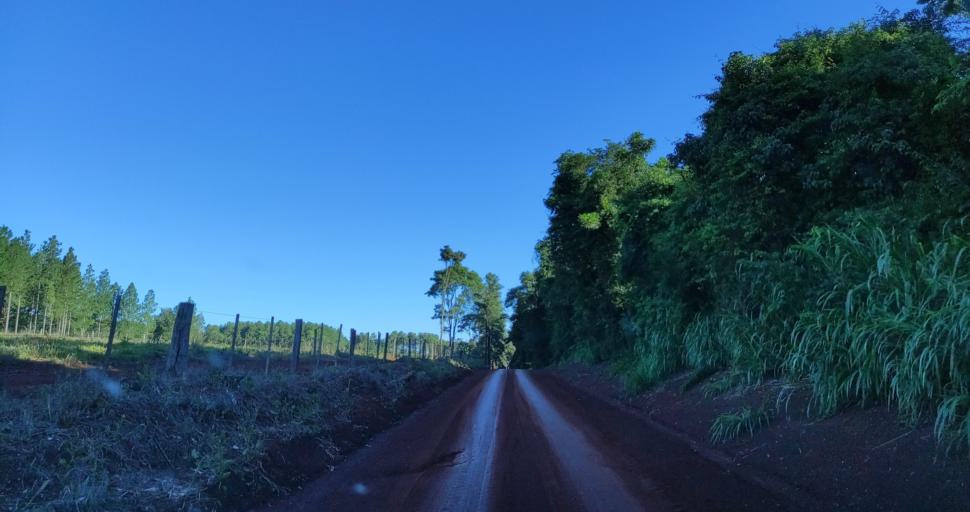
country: AR
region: Misiones
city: Puerto Rico
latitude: -26.8382
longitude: -55.0124
